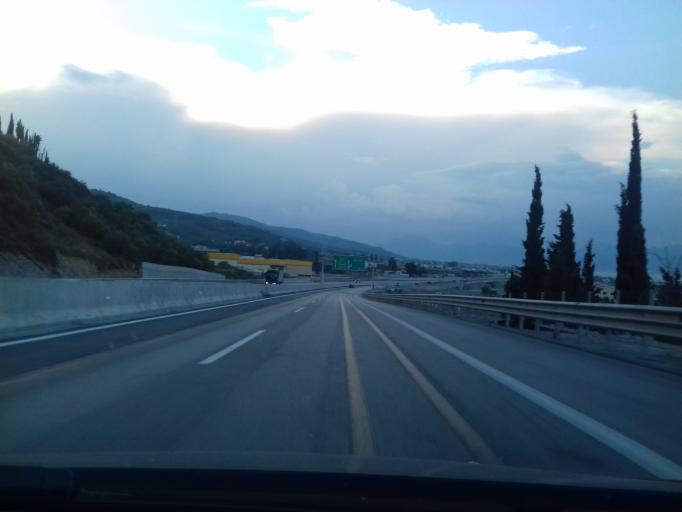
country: GR
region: West Greece
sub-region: Nomos Achaias
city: Aigio
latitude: 38.2560
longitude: 22.0658
